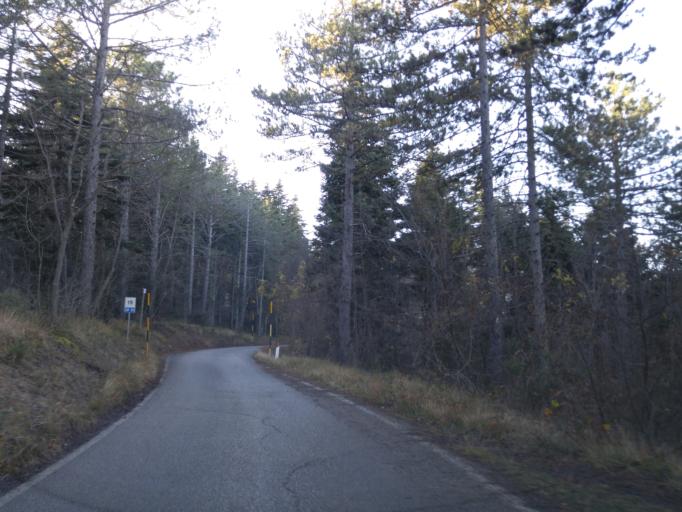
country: IT
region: The Marches
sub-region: Provincia di Pesaro e Urbino
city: Isola del Piano
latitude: 43.7017
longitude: 12.7715
